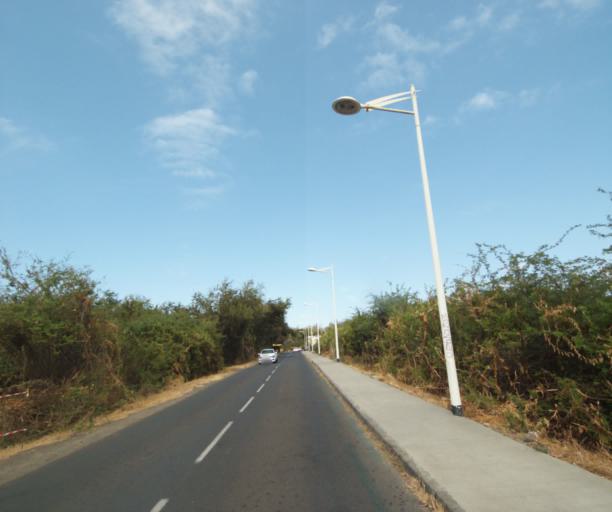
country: RE
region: Reunion
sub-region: Reunion
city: Trois-Bassins
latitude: -21.0843
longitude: 55.2335
